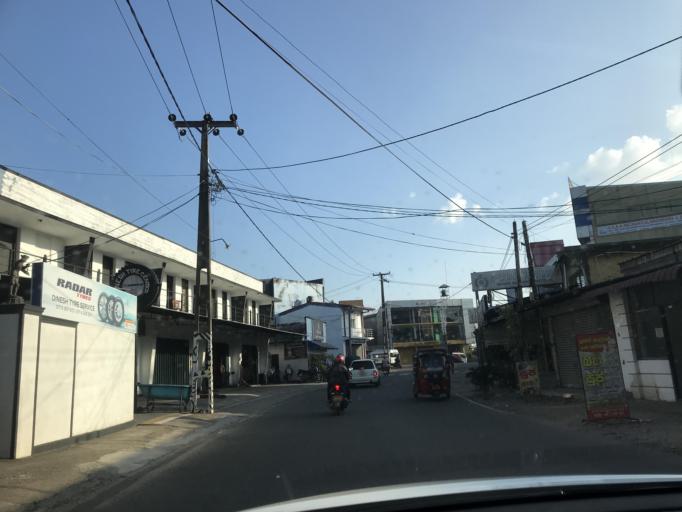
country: LK
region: Western
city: Ja Ela
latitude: 7.0856
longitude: 79.8931
